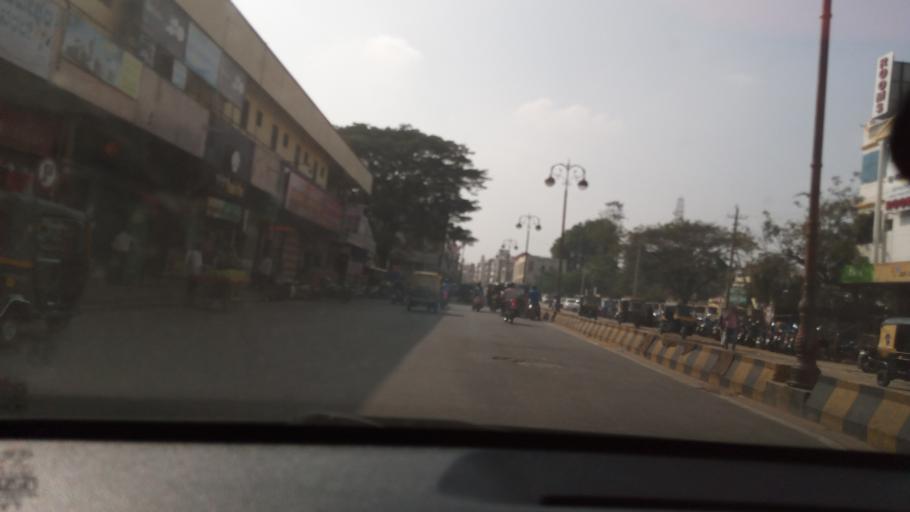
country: IN
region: Karnataka
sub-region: Mysore
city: Mysore
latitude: 12.3137
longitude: 76.6587
